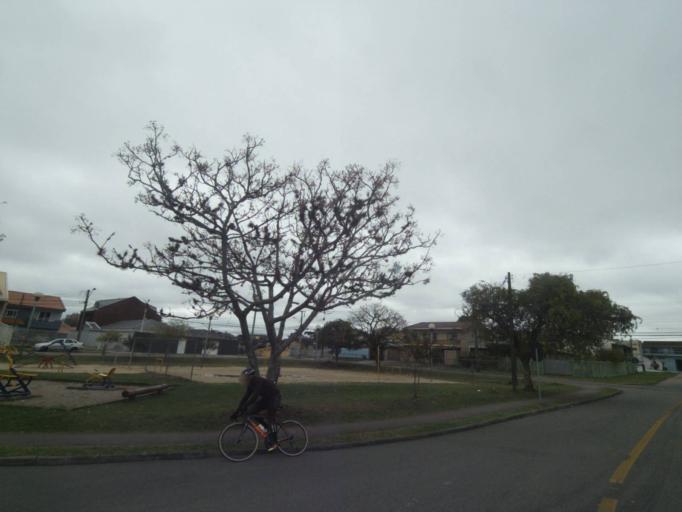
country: BR
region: Parana
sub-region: Curitiba
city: Curitiba
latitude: -25.4973
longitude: -49.2878
